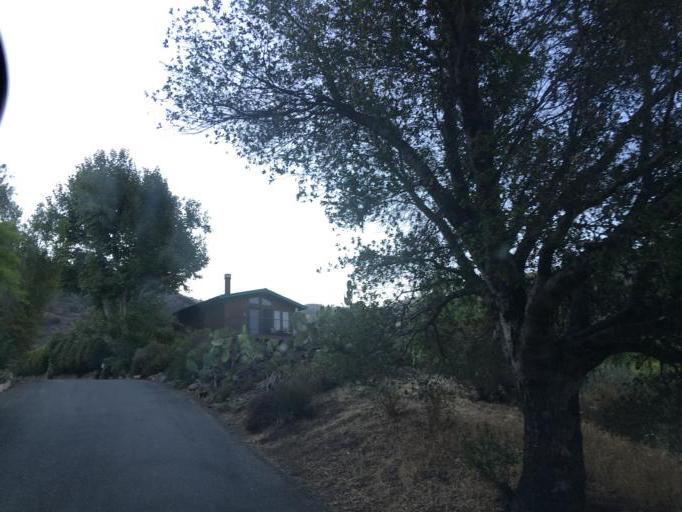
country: US
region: California
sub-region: Los Angeles County
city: Malibu Beach
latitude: 34.0797
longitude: -118.6867
